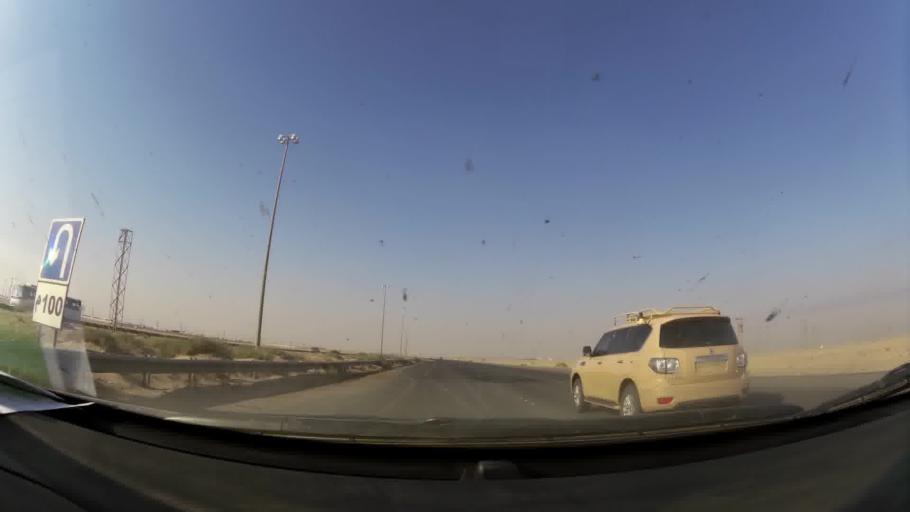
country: IQ
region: Basra Governorate
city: Umm Qasr
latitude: 29.8751
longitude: 47.6806
